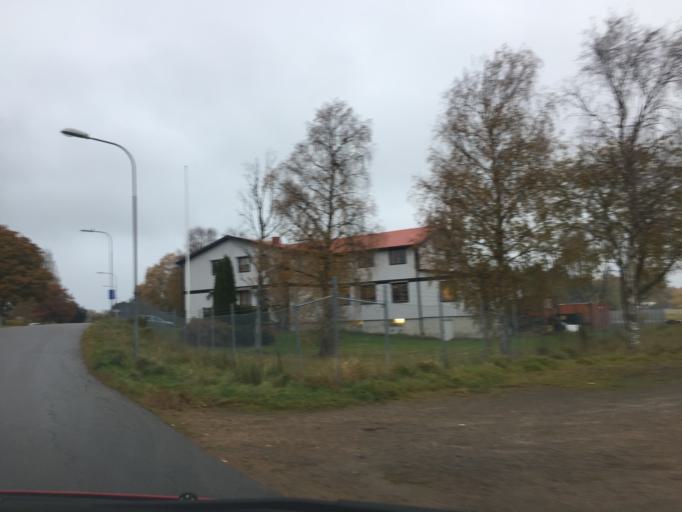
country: SE
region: Vaestra Goetaland
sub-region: Trollhattan
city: Sjuntorp
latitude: 58.1587
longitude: 12.3046
